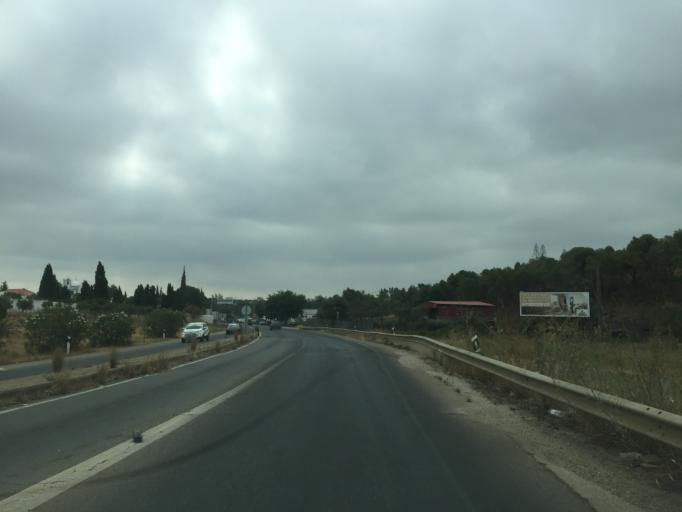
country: PT
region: Faro
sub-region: Loule
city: Almancil
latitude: 37.0831
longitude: -8.0130
